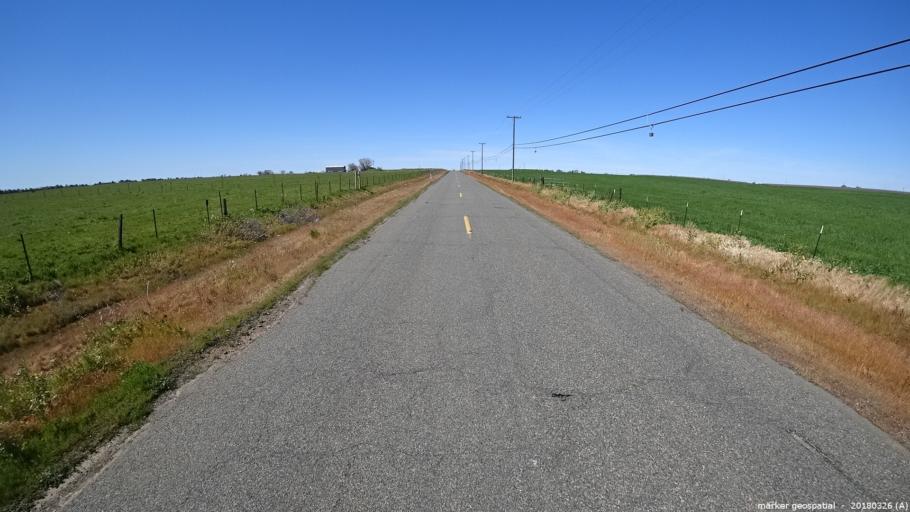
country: US
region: California
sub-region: Sacramento County
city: Wilton
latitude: 38.4690
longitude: -121.2507
